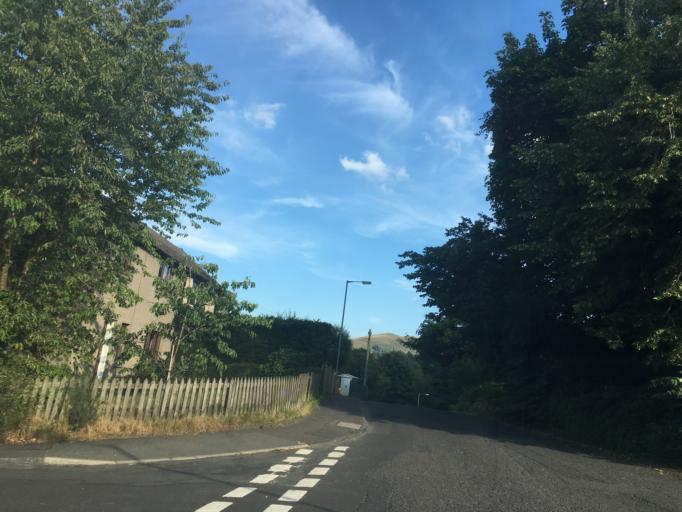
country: GB
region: Scotland
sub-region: The Scottish Borders
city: Peebles
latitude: 55.6446
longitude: -3.1859
